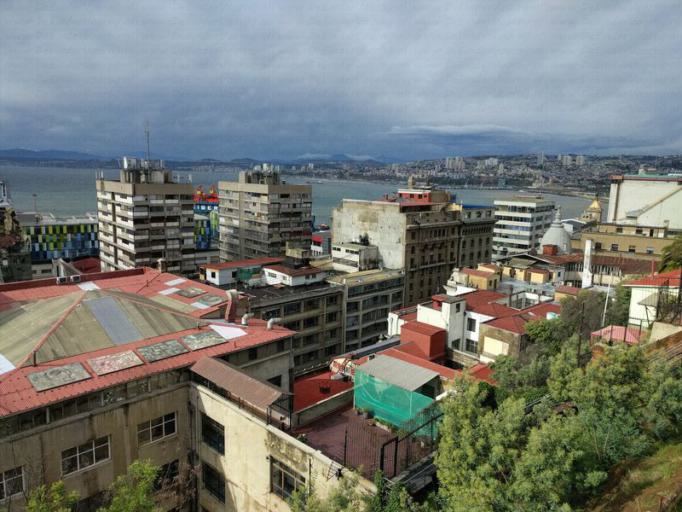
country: CL
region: Valparaiso
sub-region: Provincia de Valparaiso
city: Valparaiso
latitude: -33.0401
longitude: -71.6291
